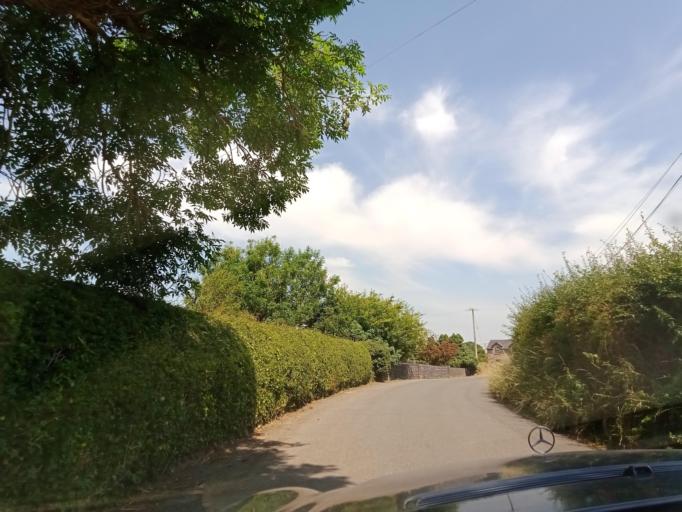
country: IE
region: Leinster
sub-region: Kilkenny
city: Mooncoin
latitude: 52.2705
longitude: -7.2337
